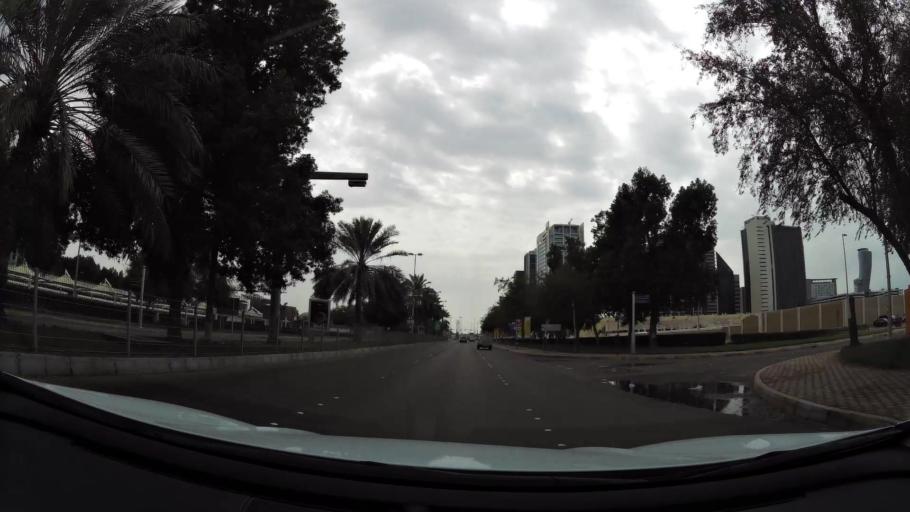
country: AE
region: Abu Dhabi
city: Abu Dhabi
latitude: 24.4235
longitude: 54.4447
